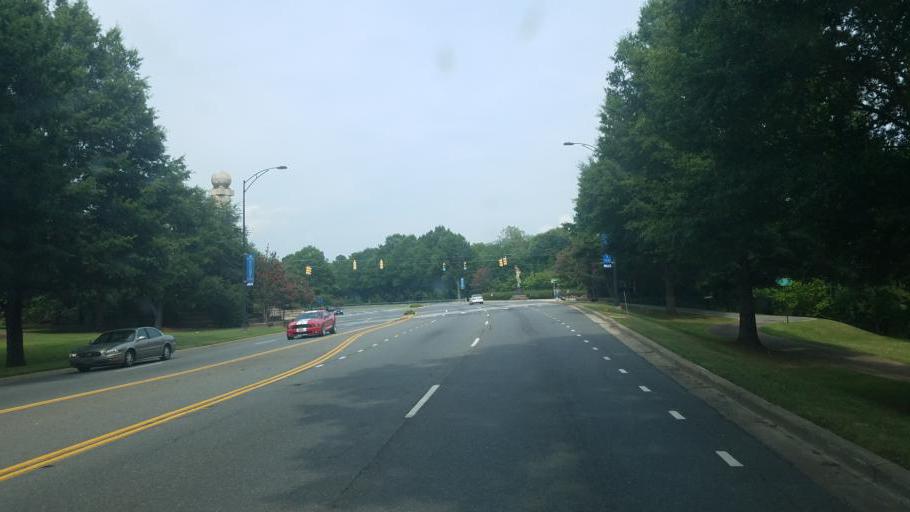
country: US
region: South Carolina
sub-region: York County
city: Rock Hill
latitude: 34.9344
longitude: -81.0043
